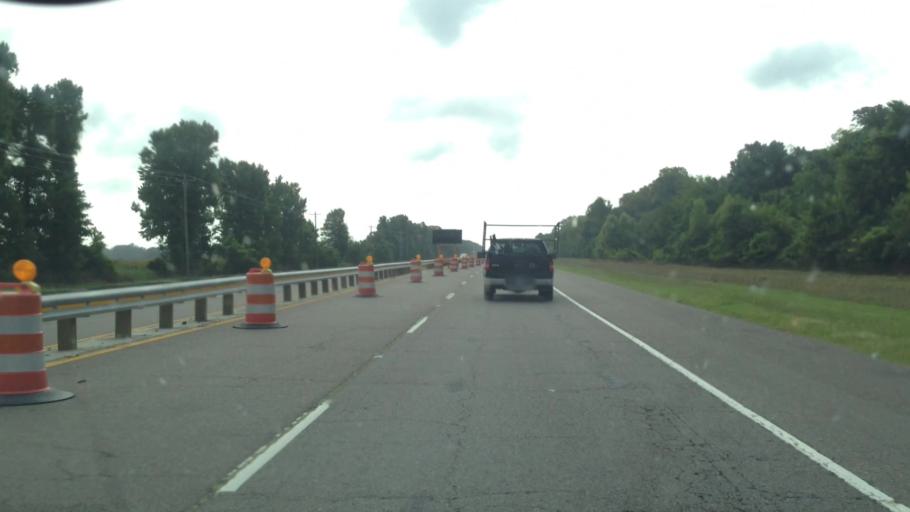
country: US
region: Louisiana
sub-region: Pointe Coupee Parish
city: Livonia
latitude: 30.5537
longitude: -91.5169
